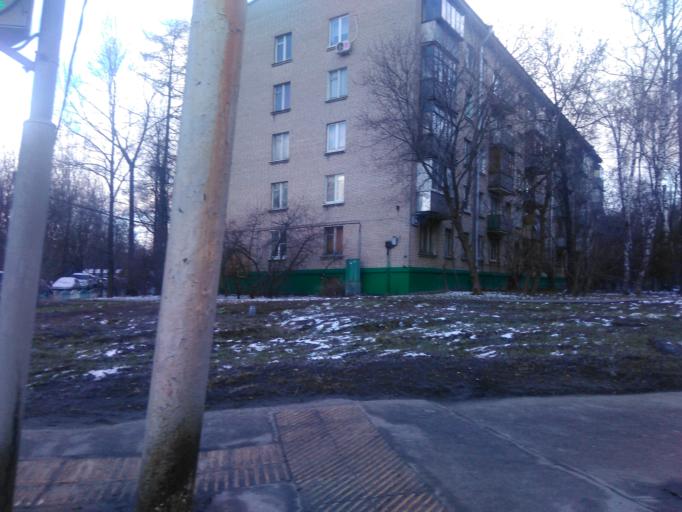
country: RU
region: Moscow
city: Tsaritsyno
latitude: 55.6477
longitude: 37.6486
